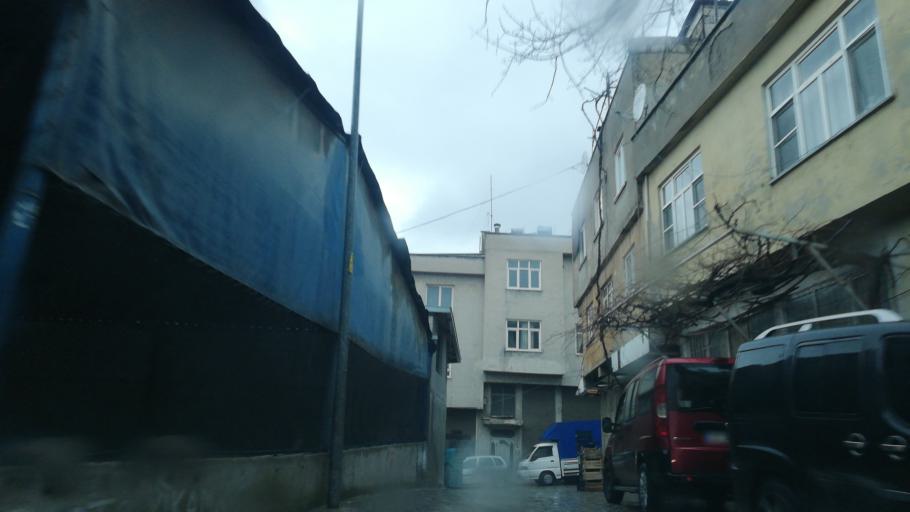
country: TR
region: Kahramanmaras
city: Kahramanmaras
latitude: 37.5825
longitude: 36.9303
